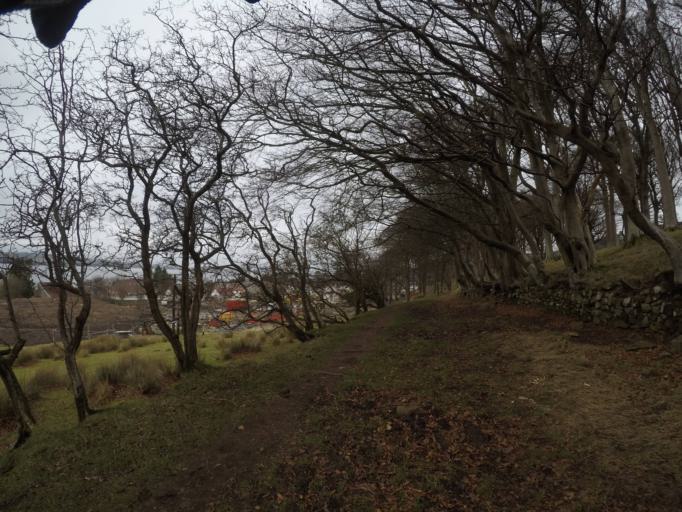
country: GB
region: Scotland
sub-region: North Ayrshire
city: Fairlie
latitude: 55.7568
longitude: -4.8499
